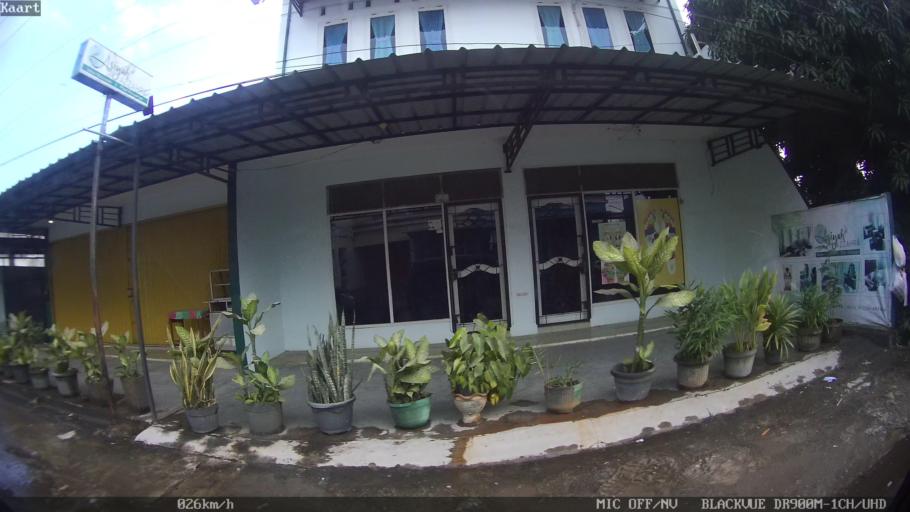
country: ID
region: Lampung
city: Kedaton
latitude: -5.3911
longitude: 105.3022
